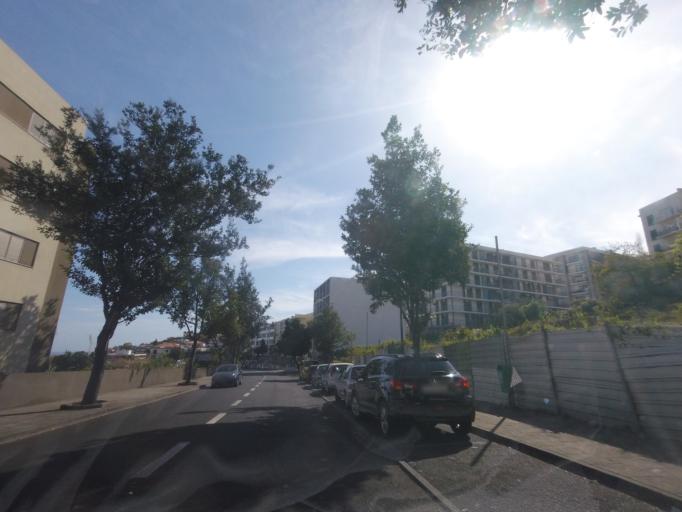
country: PT
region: Madeira
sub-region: Funchal
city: Funchal
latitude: 32.6493
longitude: -16.9300
